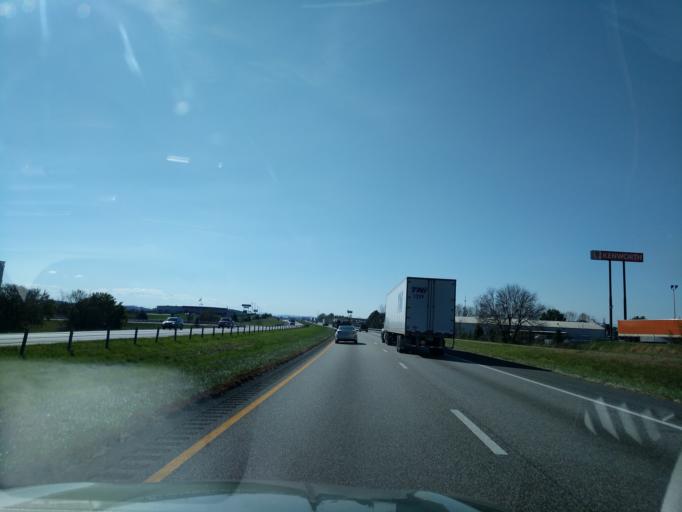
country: US
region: Virginia
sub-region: Rockingham County
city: Dayton
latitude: 38.4015
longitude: -78.9082
